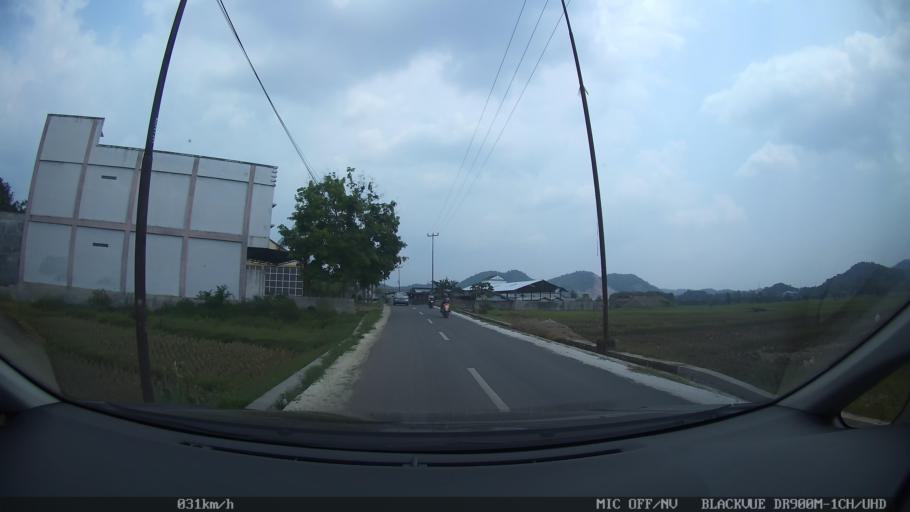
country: ID
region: Lampung
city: Gadingrejo
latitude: -5.3694
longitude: 105.0270
